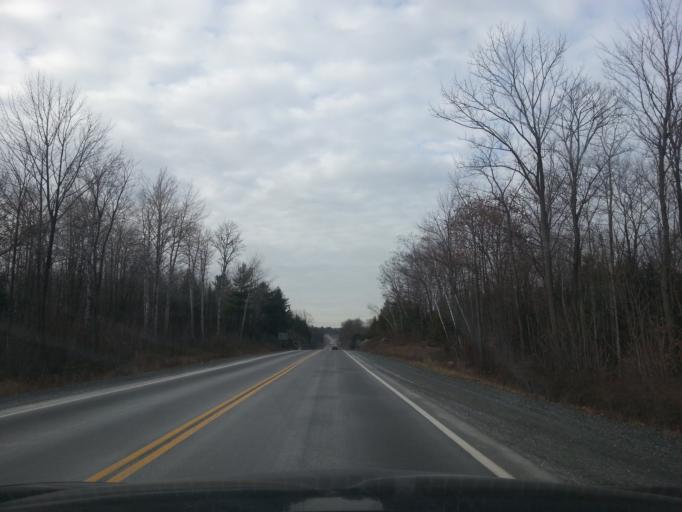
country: CA
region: Ontario
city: Quinte West
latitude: 44.4659
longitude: -77.7273
